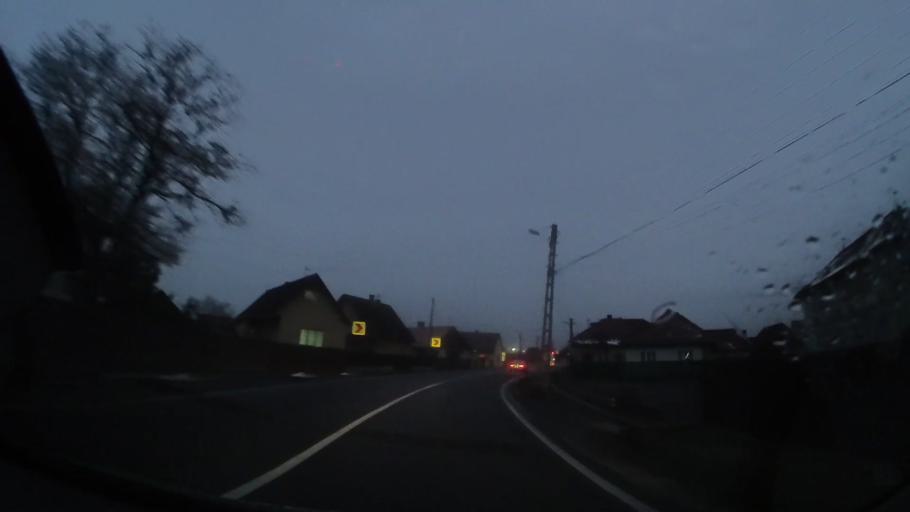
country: RO
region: Harghita
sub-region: Comuna Ditrau
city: Ditrau
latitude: 46.8059
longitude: 25.4936
